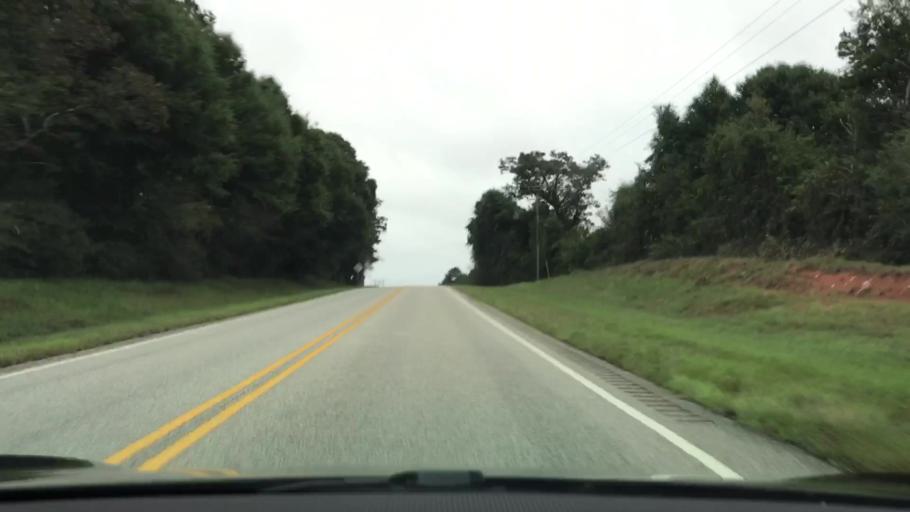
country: US
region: Alabama
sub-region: Coffee County
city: Elba
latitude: 31.3634
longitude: -86.1134
